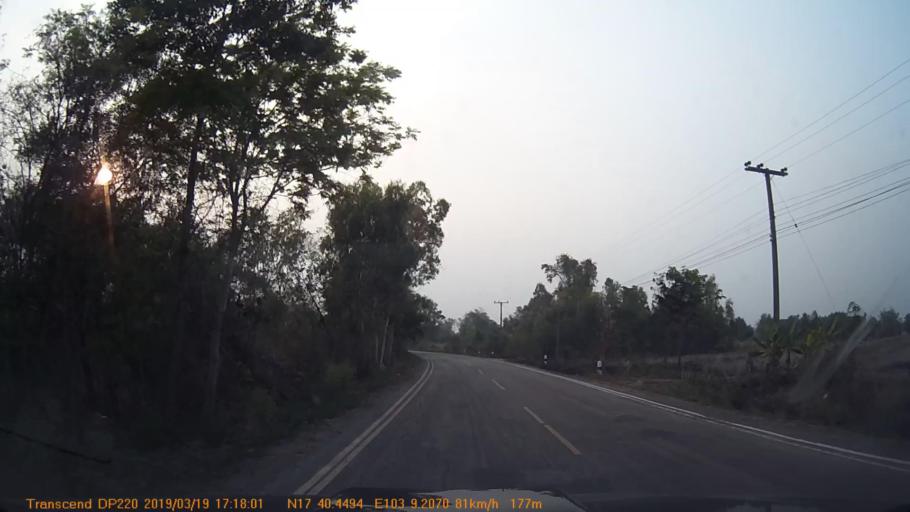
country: TH
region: Changwat Udon Thani
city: Ban Dung
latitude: 17.6745
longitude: 103.1528
